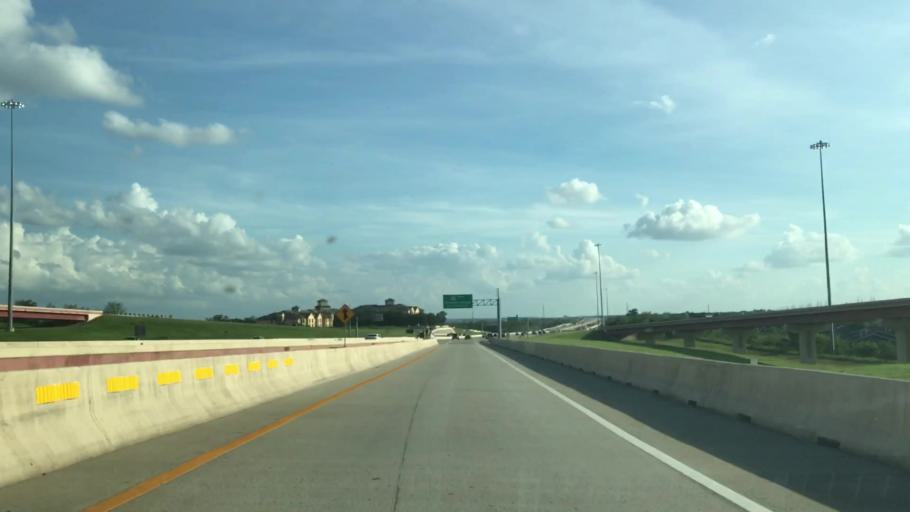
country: US
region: Texas
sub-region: Tarrant County
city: Euless
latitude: 32.8344
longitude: -97.0171
